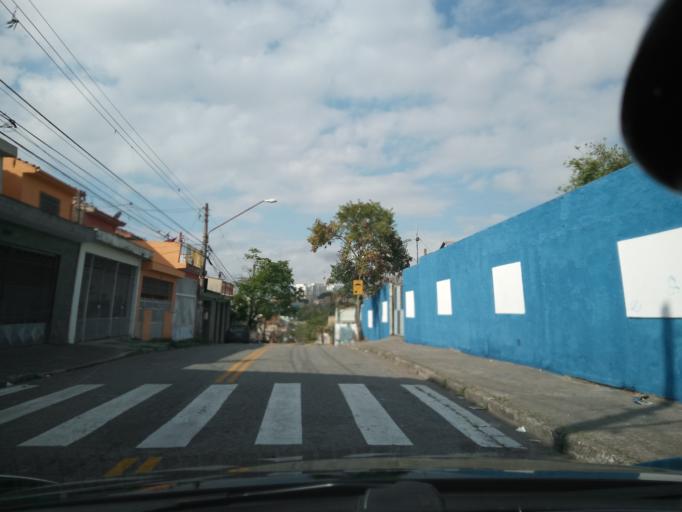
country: BR
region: Sao Paulo
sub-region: Sao Bernardo Do Campo
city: Sao Bernardo do Campo
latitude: -23.7025
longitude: -46.5666
